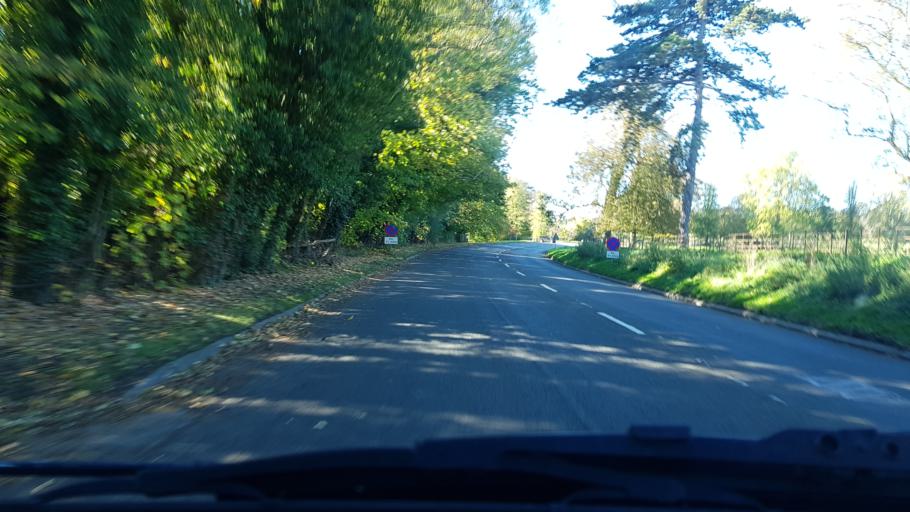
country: GB
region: England
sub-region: Surrey
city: East Horsley
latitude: 51.2210
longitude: -0.4554
